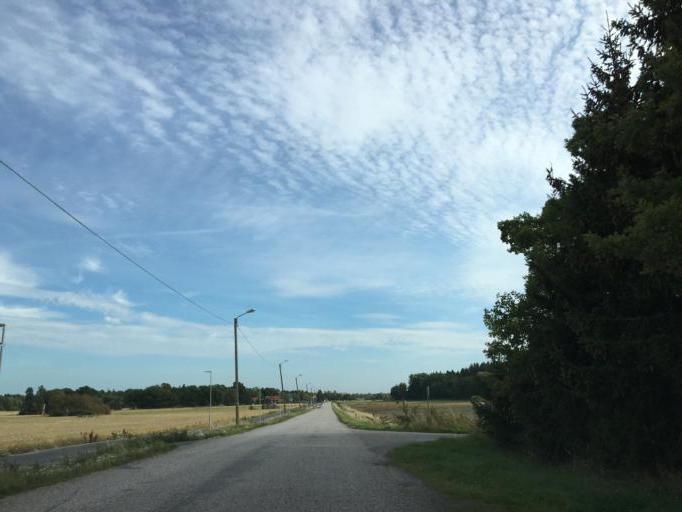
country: SE
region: Soedermanland
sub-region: Eskilstuna Kommun
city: Torshalla
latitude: 59.4440
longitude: 16.4701
